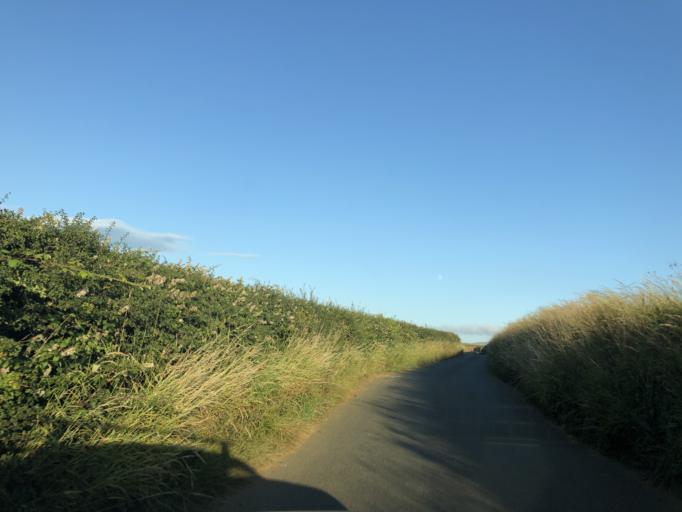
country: GB
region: England
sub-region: Isle of Wight
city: Chale
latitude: 50.6383
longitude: -1.3583
